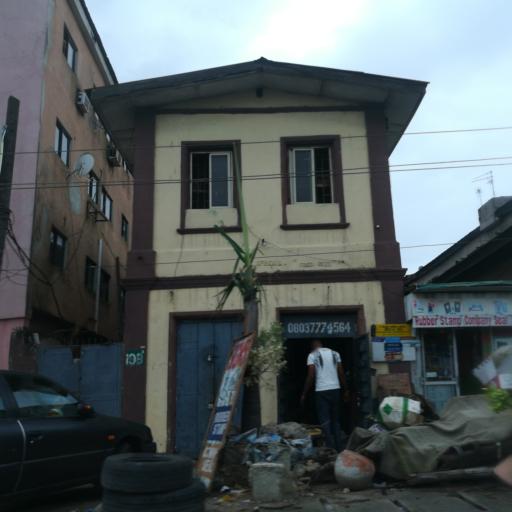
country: NG
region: Lagos
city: Makoko
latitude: 6.4935
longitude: 3.3784
